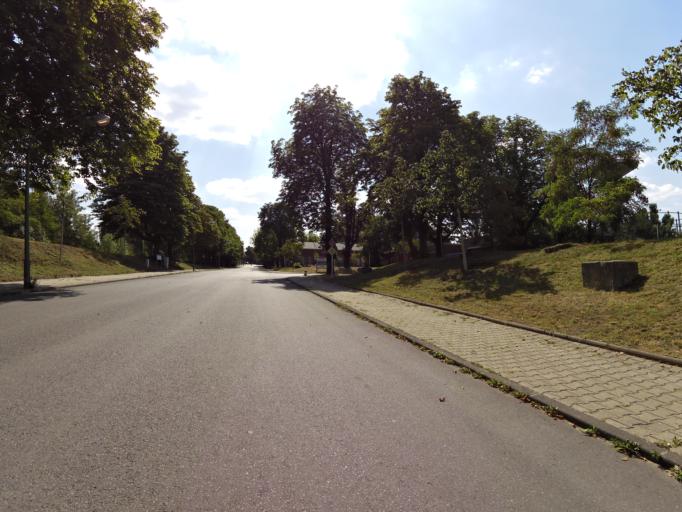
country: DE
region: Berlin
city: Mariendorf
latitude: 52.4393
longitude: 13.3720
